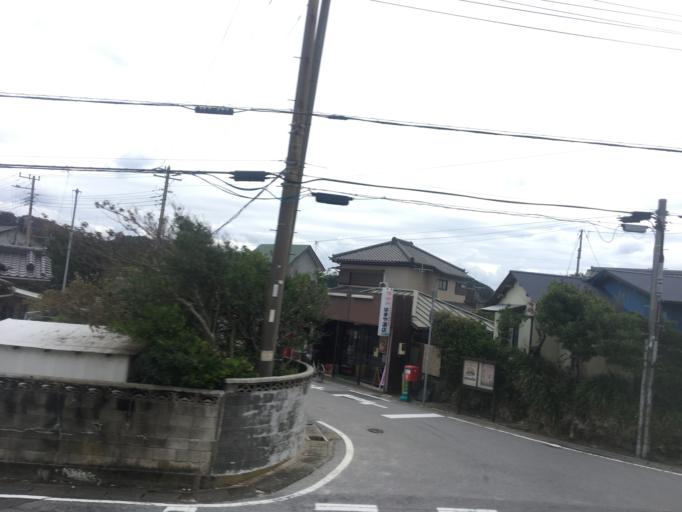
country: JP
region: Chiba
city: Katsuura
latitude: 35.1390
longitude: 140.2607
